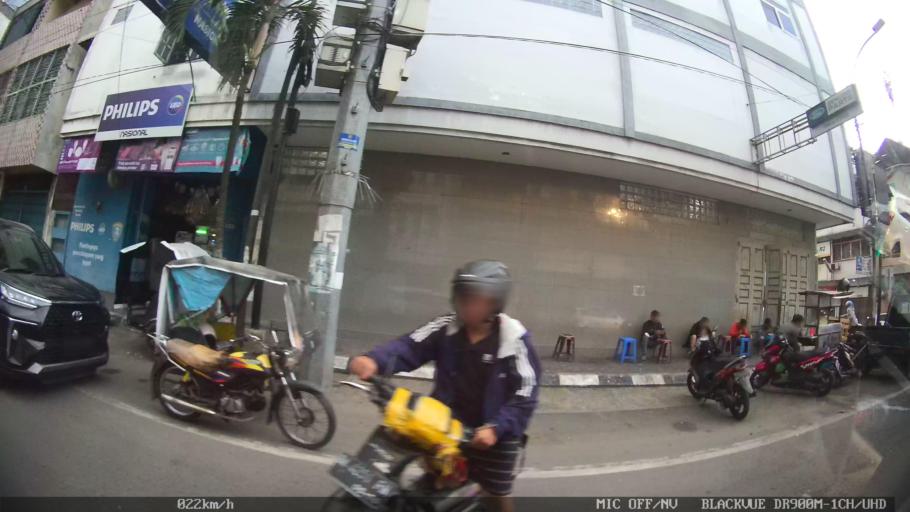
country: ID
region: North Sumatra
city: Medan
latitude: 3.5839
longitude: 98.6864
